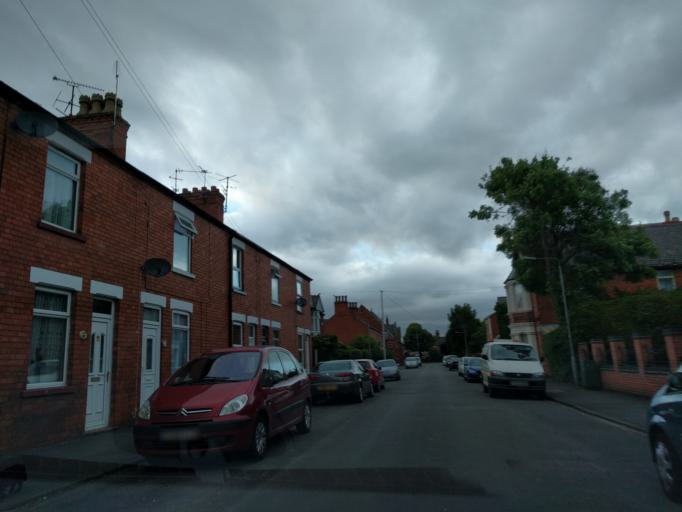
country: GB
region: England
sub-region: Nottinghamshire
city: Newark on Trent
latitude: 53.0701
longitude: -0.8029
